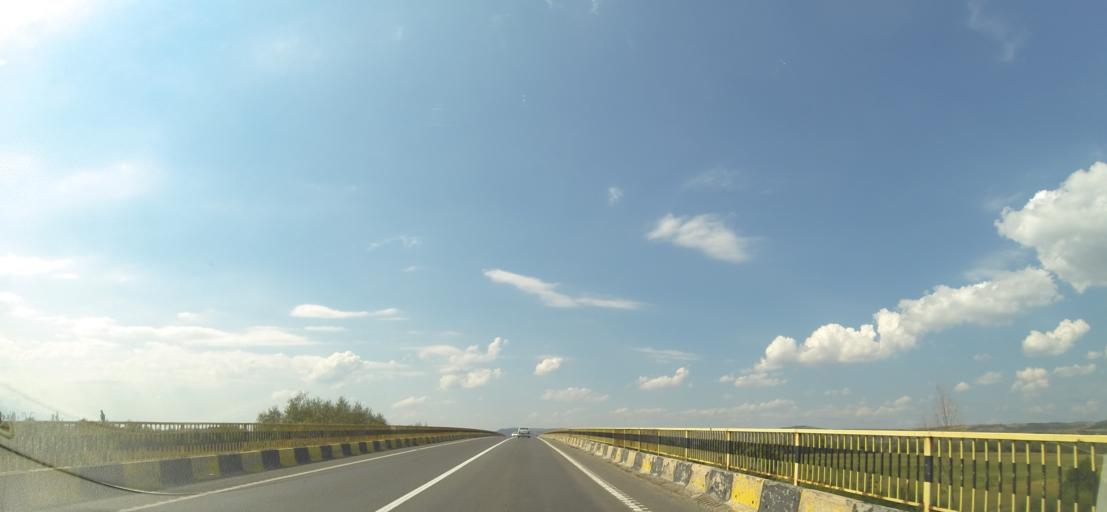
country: RO
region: Brasov
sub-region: Comuna Mandra
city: Mandra
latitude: 45.8308
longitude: 25.0189
